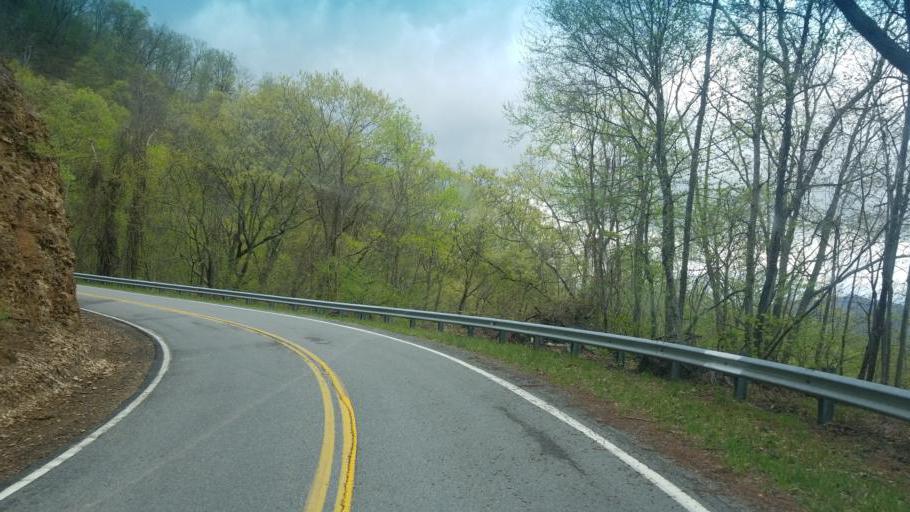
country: US
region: Virginia
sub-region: Tazewell County
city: Tazewell
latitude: 37.0035
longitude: -81.5254
